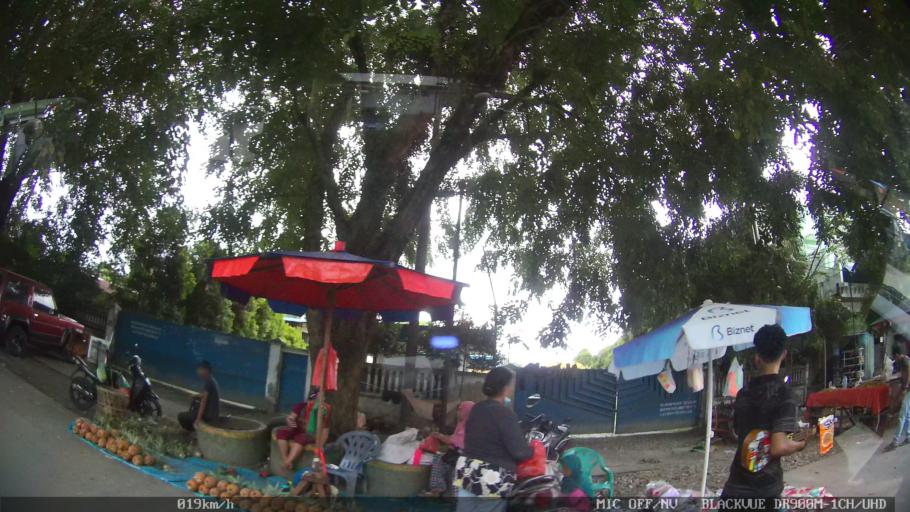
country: ID
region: North Sumatra
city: Sunggal
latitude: 3.6011
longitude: 98.6083
